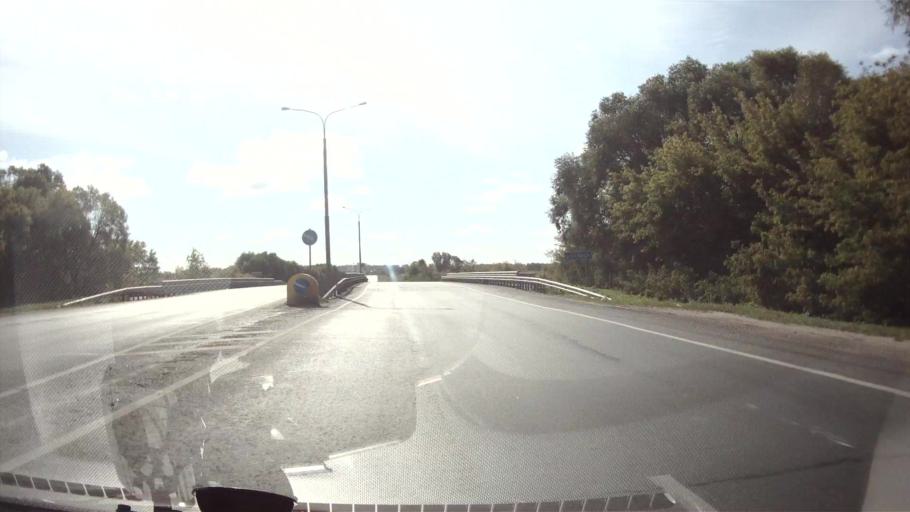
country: RU
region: Ulyanovsk
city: Isheyevka
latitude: 54.3048
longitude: 48.2416
